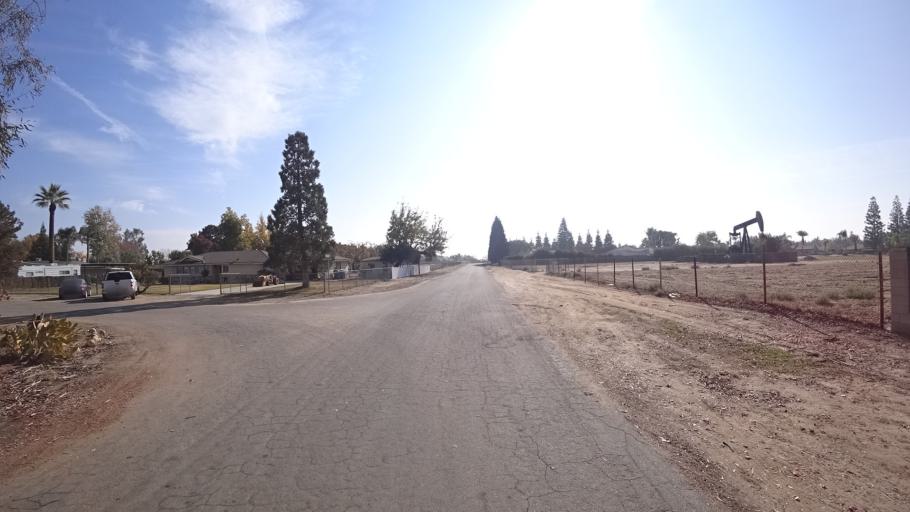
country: US
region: California
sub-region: Kern County
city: Rosedale
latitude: 35.3637
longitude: -119.1721
